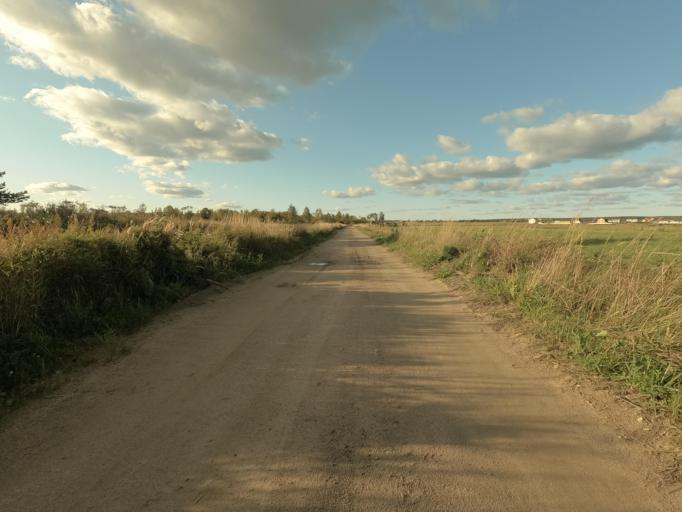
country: RU
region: Leningrad
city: Imeni Sverdlova
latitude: 59.8636
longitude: 30.7304
